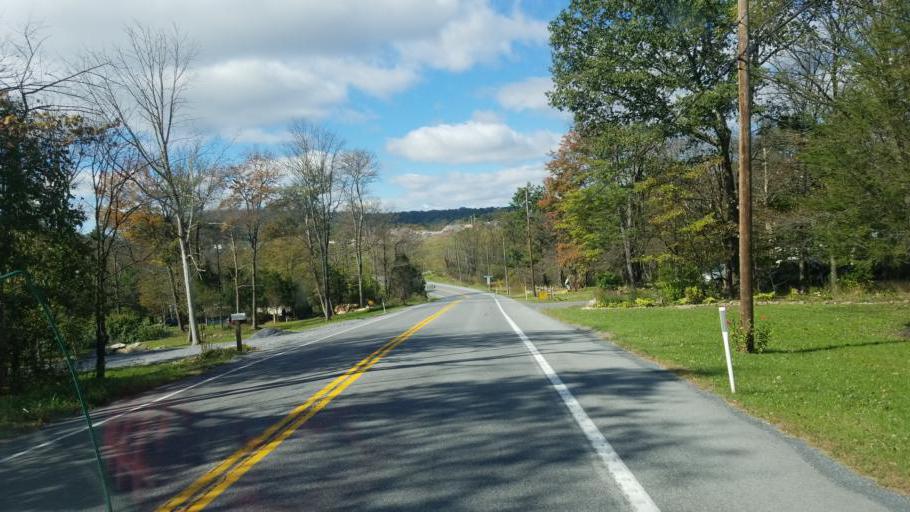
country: US
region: Pennsylvania
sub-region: Bedford County
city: Earlston
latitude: 40.0204
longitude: -78.1824
